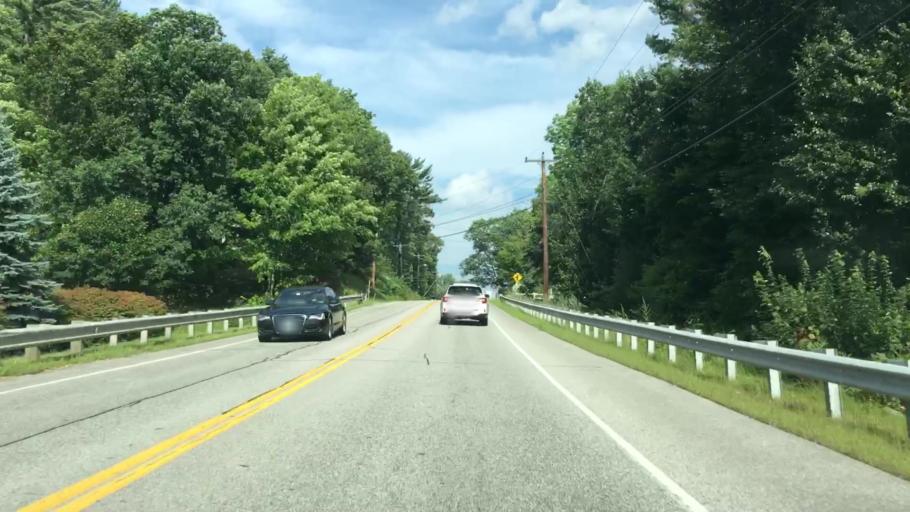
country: US
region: New Hampshire
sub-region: Belknap County
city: Sanbornton
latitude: 43.4851
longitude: -71.5353
